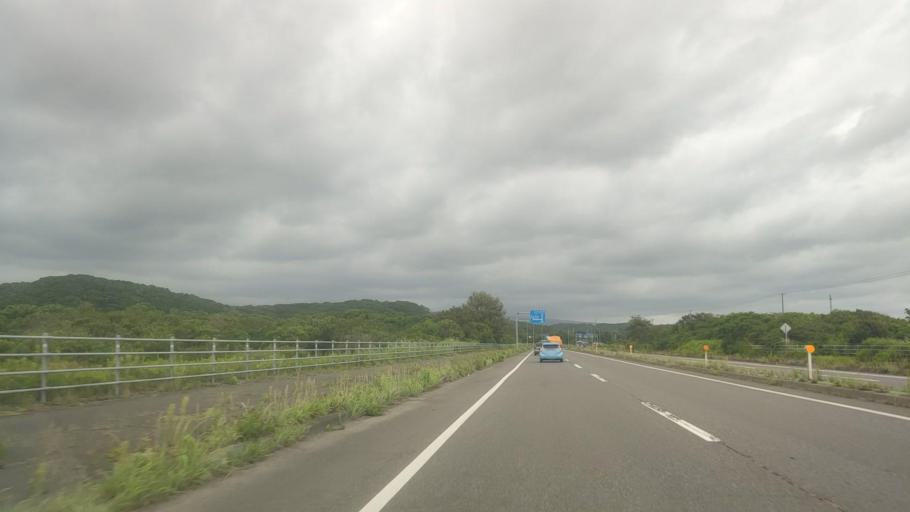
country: JP
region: Hokkaido
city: Shiraoi
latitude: 42.5599
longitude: 141.3805
